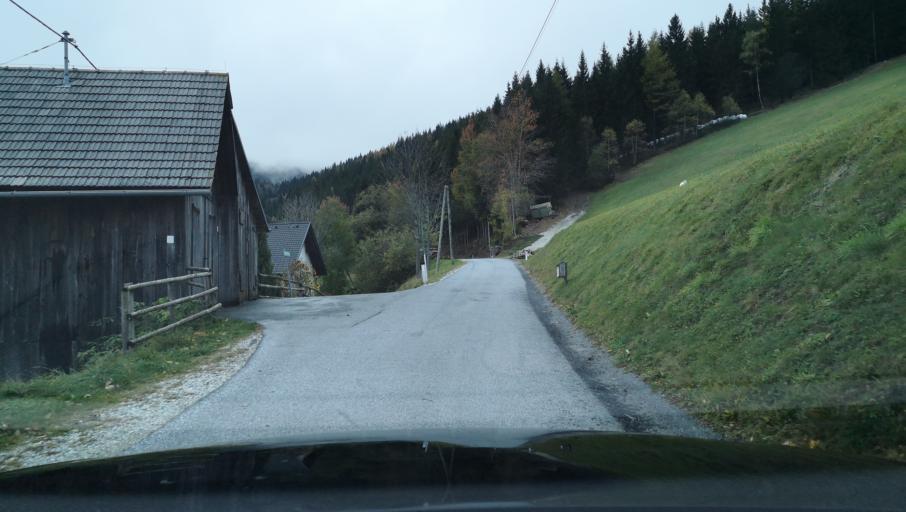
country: AT
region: Styria
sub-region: Politischer Bezirk Weiz
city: Gasen
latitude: 47.3596
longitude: 15.6024
